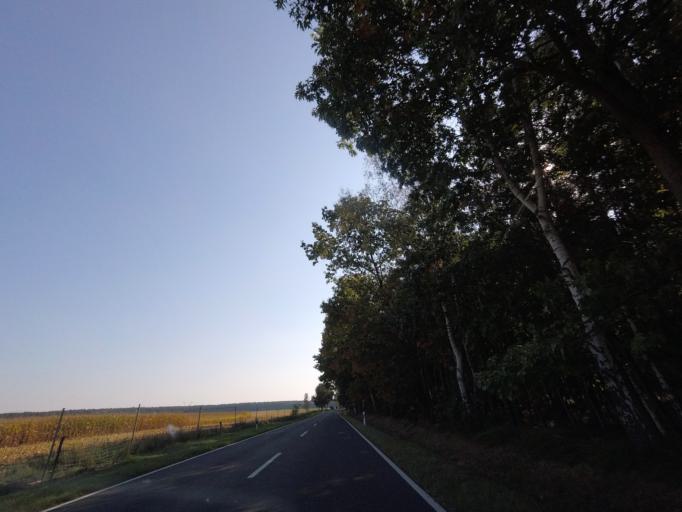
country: DE
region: Brandenburg
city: Niedergorsdorf
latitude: 51.8891
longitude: 13.0254
